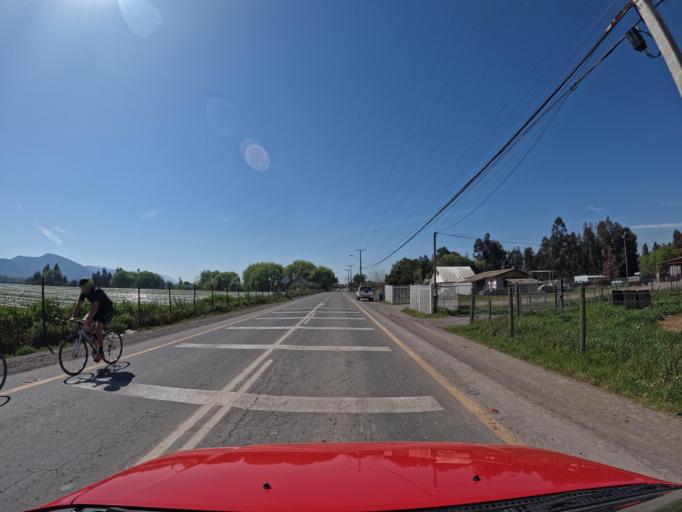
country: CL
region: Maule
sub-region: Provincia de Curico
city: Rauco
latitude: -35.0034
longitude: -71.3990
